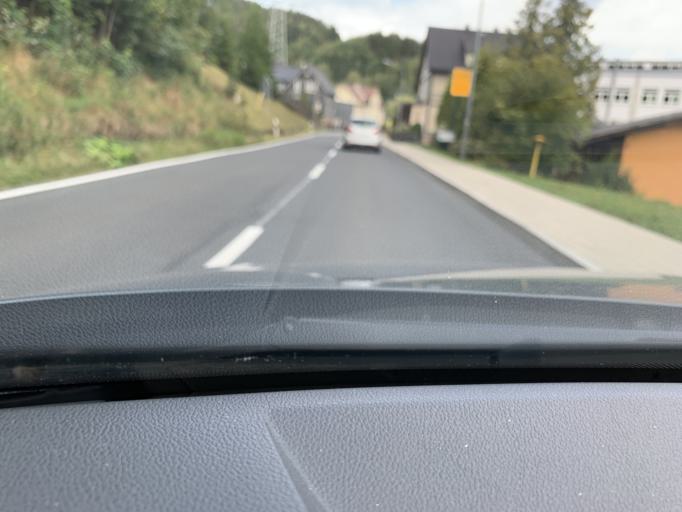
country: DE
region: Thuringia
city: Steinach
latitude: 50.4201
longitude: 11.1689
